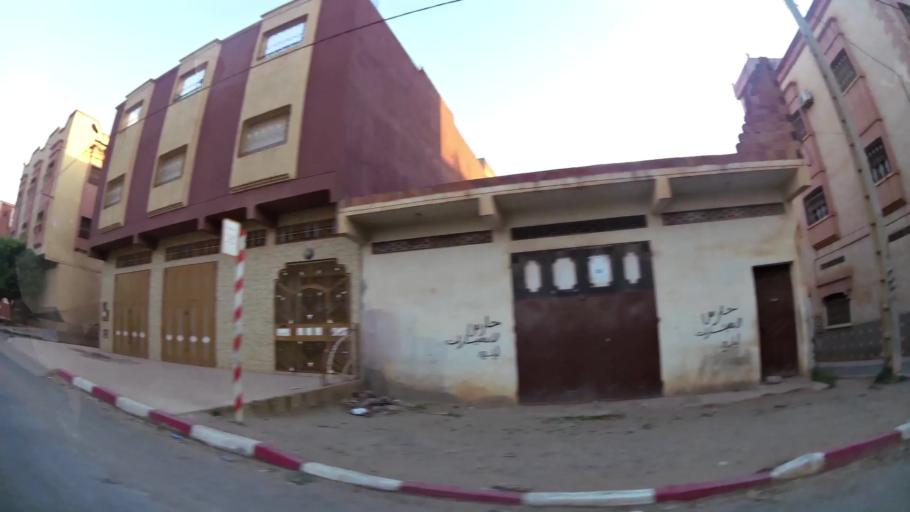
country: MA
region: Oriental
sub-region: Berkane-Taourirt
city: Berkane
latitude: 34.9119
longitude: -2.3177
